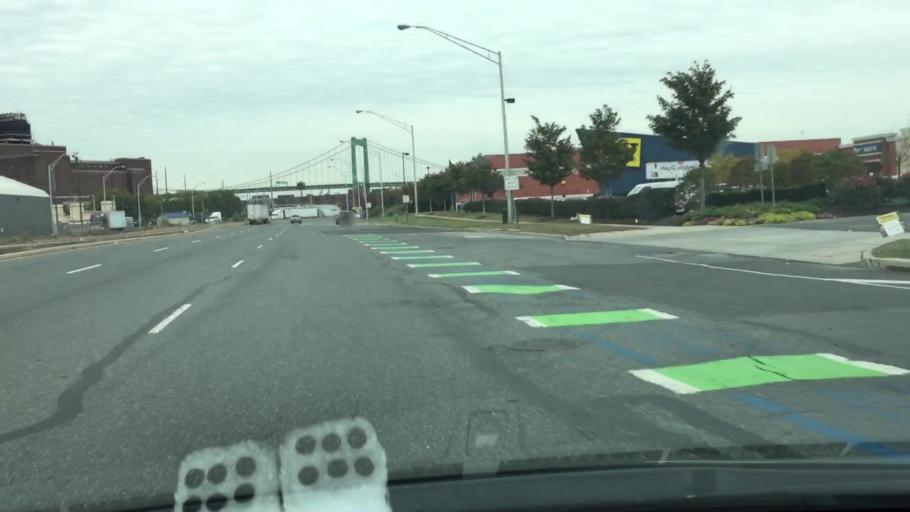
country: US
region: New Jersey
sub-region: Camden County
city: Camden
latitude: 39.9173
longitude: -75.1391
